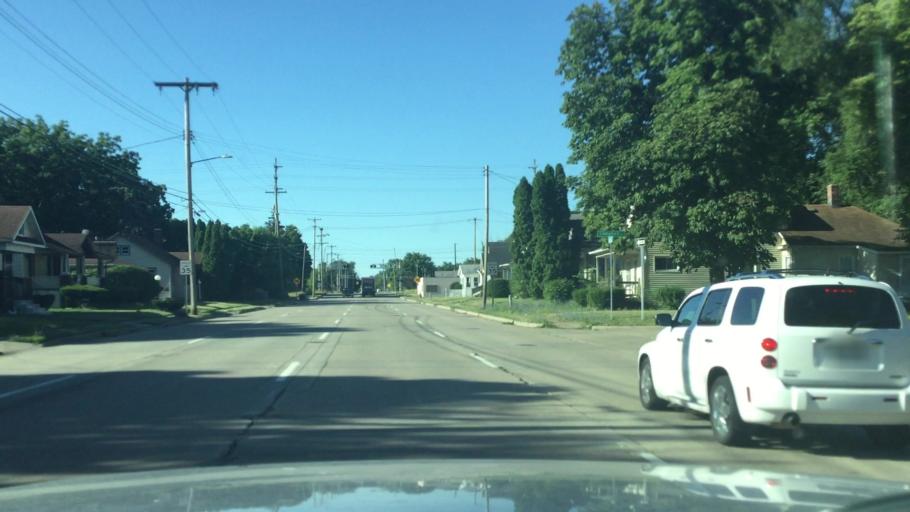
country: US
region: Michigan
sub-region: Saginaw County
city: Saginaw
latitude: 43.4144
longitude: -83.9360
